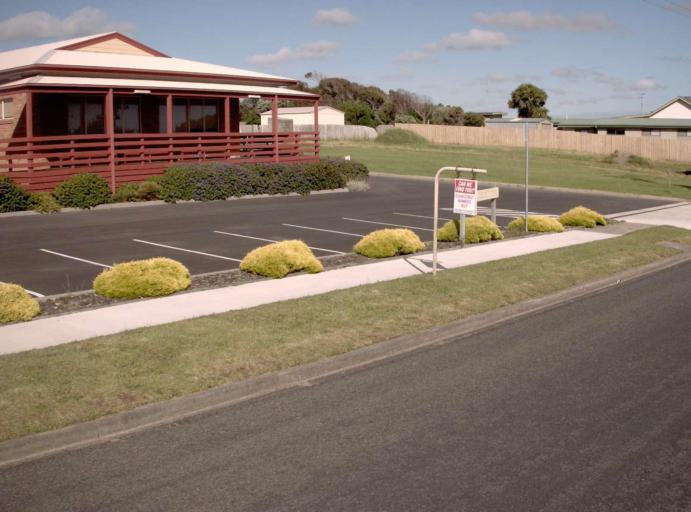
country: AU
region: Victoria
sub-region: Bass Coast
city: North Wonthaggi
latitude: -38.5486
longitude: 145.4747
